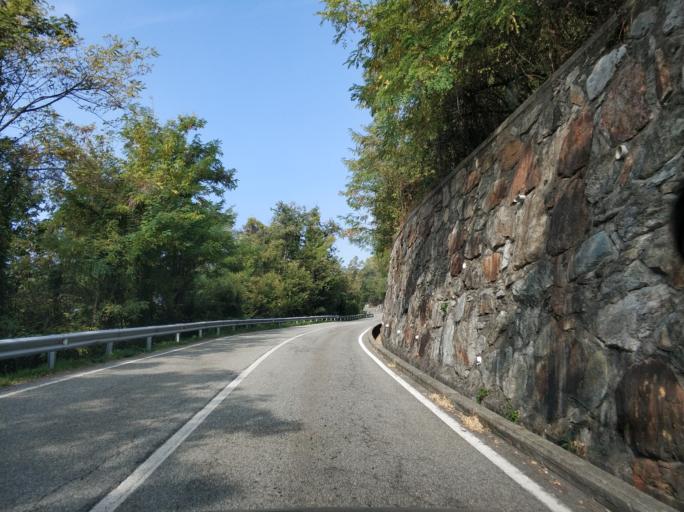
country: IT
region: Piedmont
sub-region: Provincia di Torino
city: Chiaverano
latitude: 45.5119
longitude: 7.9032
